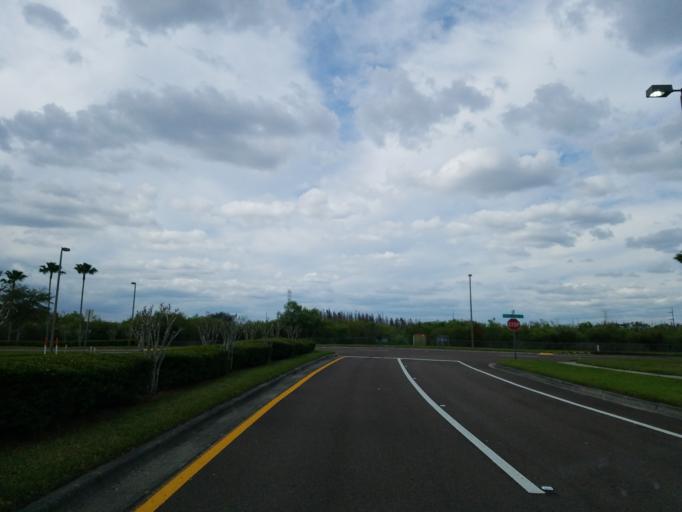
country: US
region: Florida
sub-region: Hillsborough County
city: Palm River-Clair Mel
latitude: 27.9339
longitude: -82.3447
